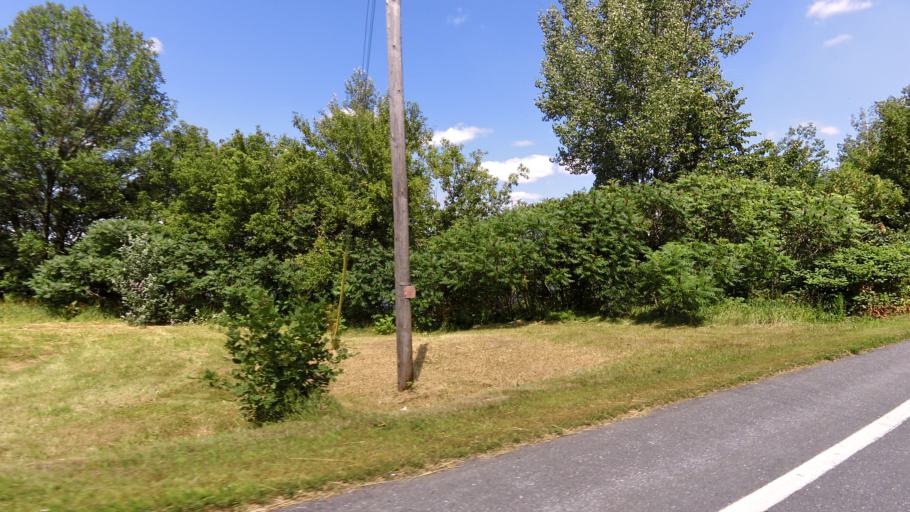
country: CA
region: Quebec
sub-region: Monteregie
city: Richelieu
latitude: 45.4076
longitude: -73.2479
